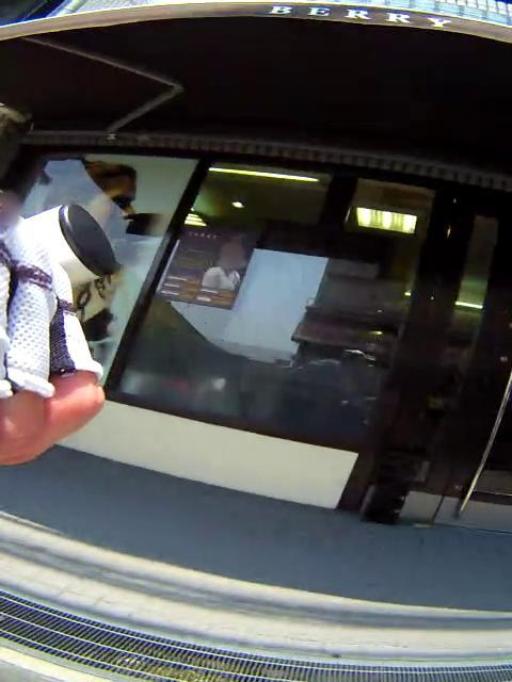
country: JP
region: Osaka
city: Suita
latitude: 34.7640
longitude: 135.5069
